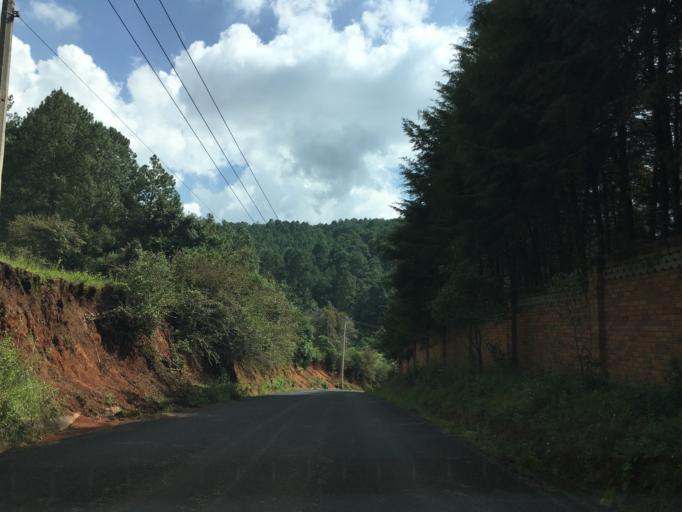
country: MX
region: Michoacan
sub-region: Morelia
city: Morelos
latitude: 19.5684
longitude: -101.1892
